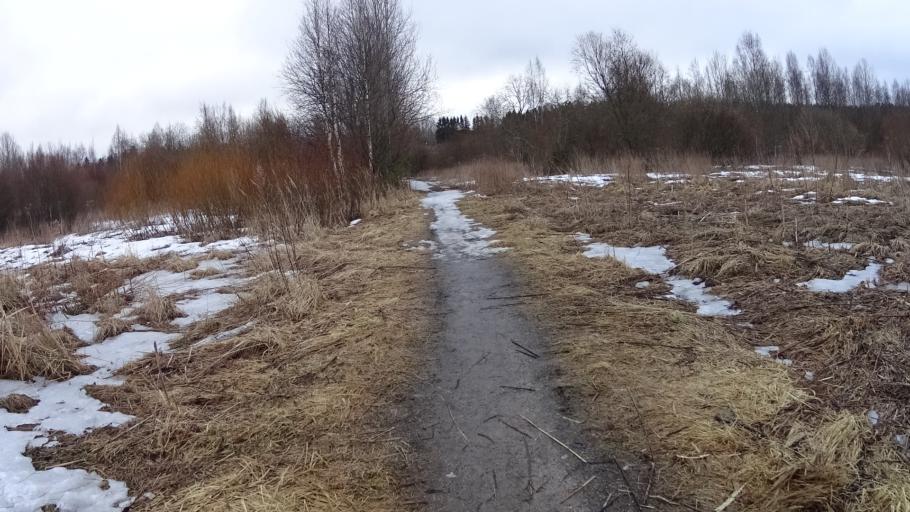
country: FI
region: Uusimaa
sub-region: Helsinki
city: Kilo
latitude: 60.2394
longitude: 24.7816
